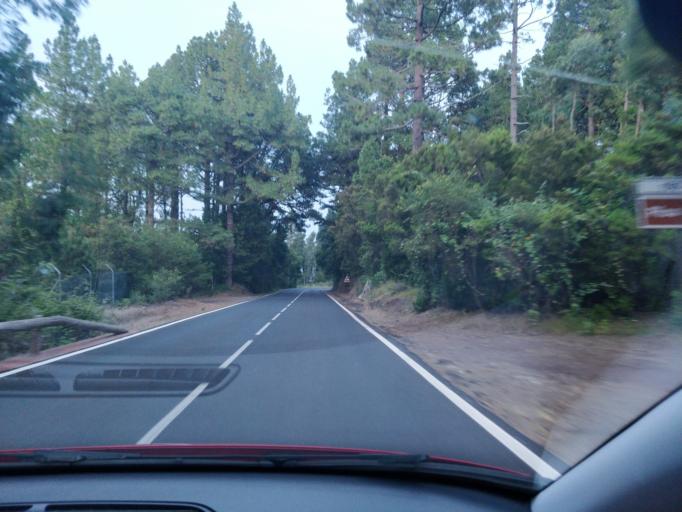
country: ES
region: Canary Islands
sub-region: Provincia de Santa Cruz de Tenerife
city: Sauzal
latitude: 28.4296
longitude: -16.3956
